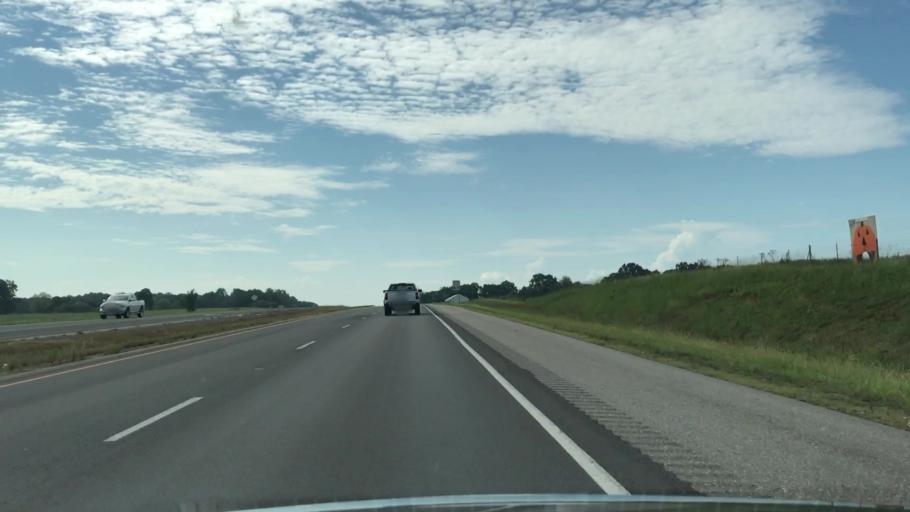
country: US
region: Kentucky
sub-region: Warren County
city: Plano
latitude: 36.8235
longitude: -86.3104
